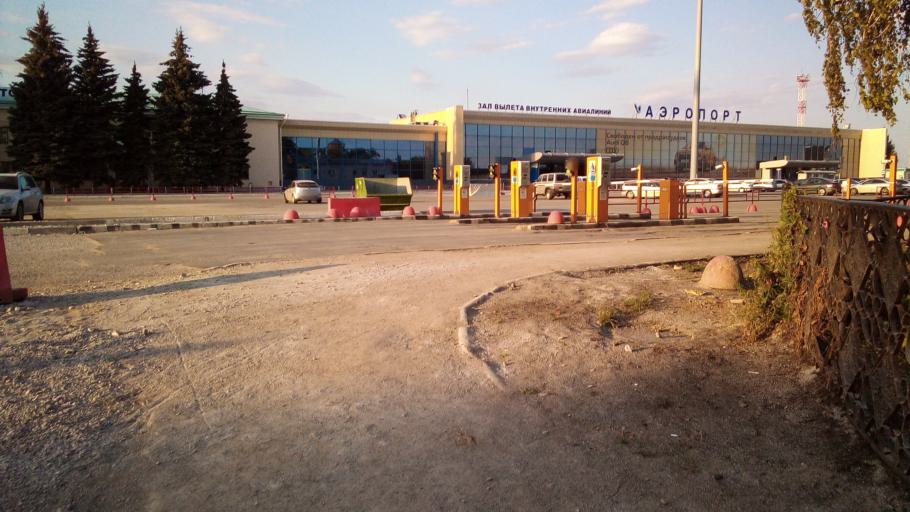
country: RU
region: Chelyabinsk
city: Potanino
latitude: 55.2970
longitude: 61.5124
